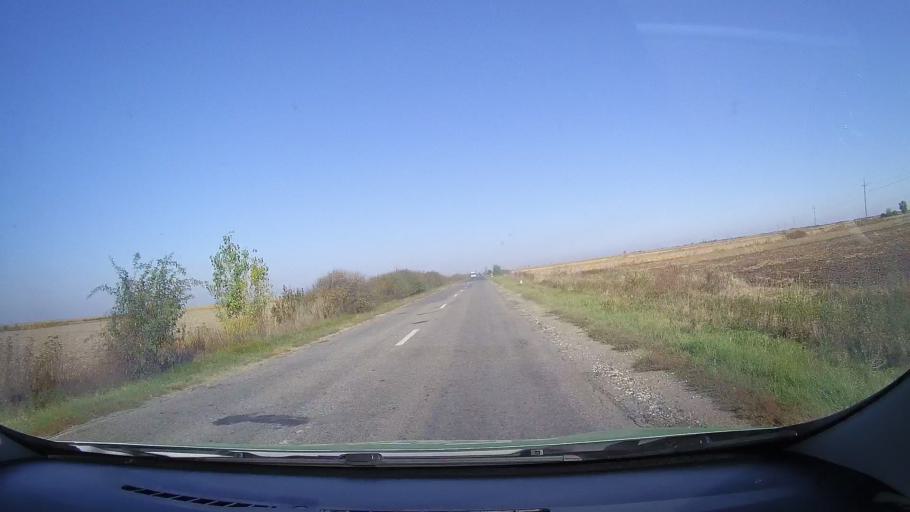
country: RO
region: Satu Mare
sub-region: Oras Tasnad
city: Tasnad
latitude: 47.5173
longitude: 22.5716
